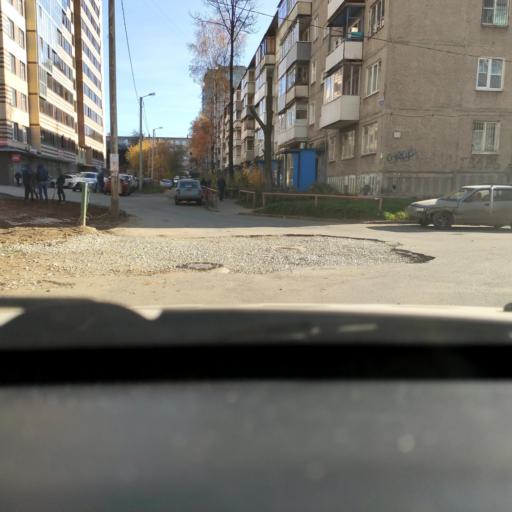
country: RU
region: Perm
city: Perm
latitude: 58.0090
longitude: 56.2067
